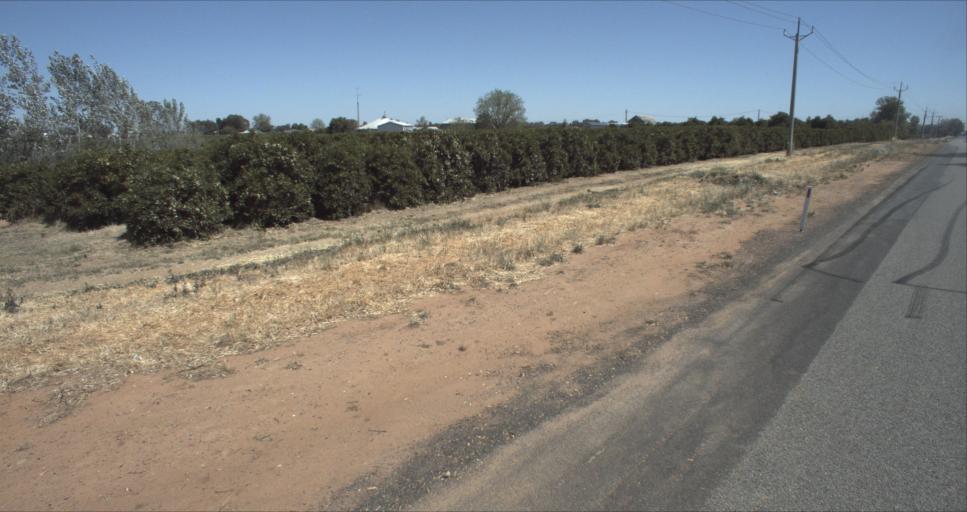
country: AU
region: New South Wales
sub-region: Leeton
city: Leeton
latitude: -34.5332
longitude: 146.3985
